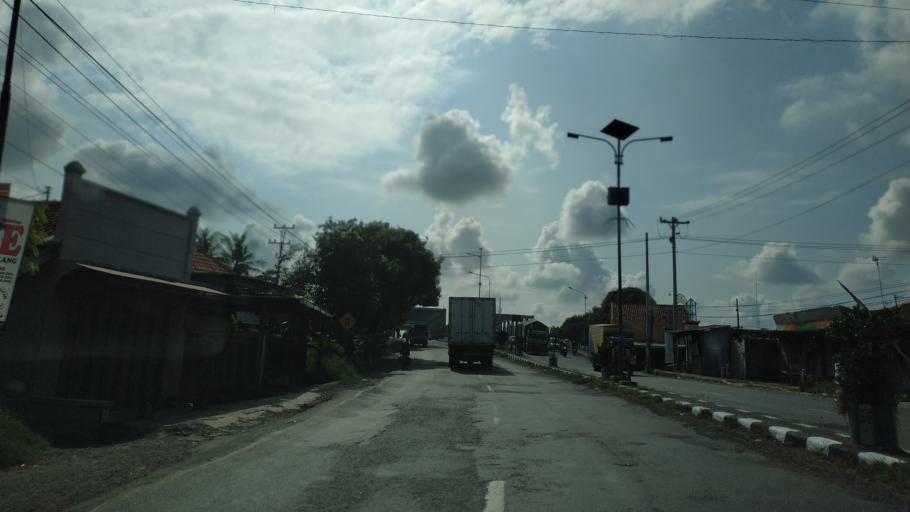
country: ID
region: Central Java
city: Comal
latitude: -6.9001
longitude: 109.5233
